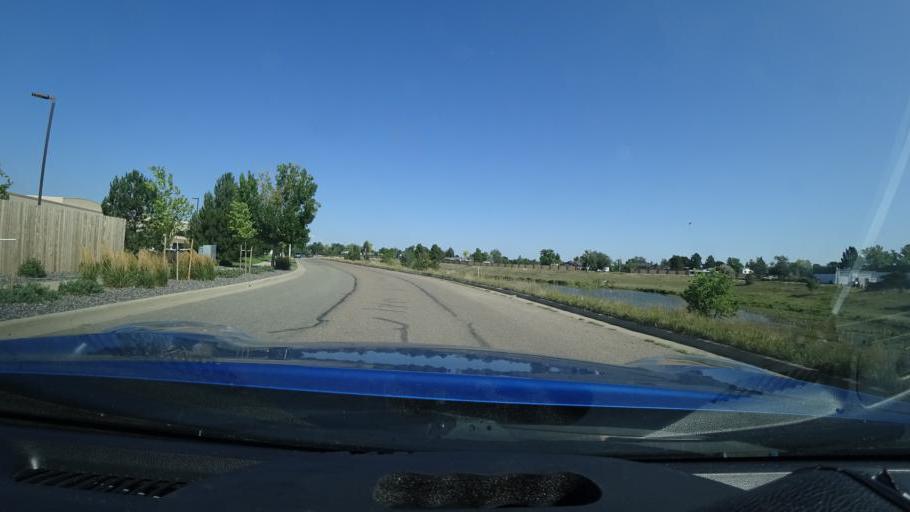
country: US
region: Colorado
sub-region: Adams County
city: Aurora
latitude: 39.7238
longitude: -104.7960
